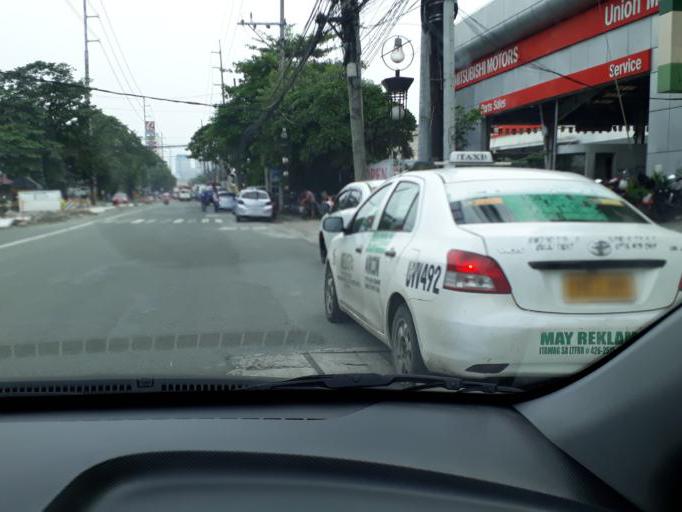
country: PH
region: Metro Manila
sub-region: City of Manila
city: Quiapo
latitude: 14.5897
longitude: 120.9973
